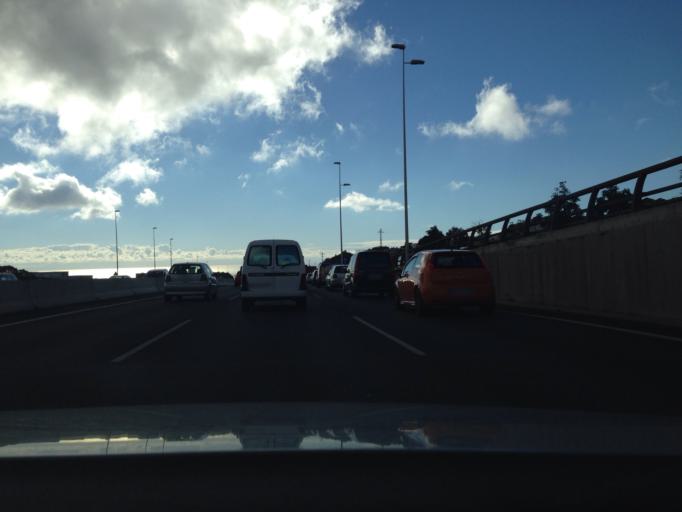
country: ES
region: Canary Islands
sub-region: Provincia de Santa Cruz de Tenerife
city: La Laguna
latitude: 28.4797
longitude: -16.3173
